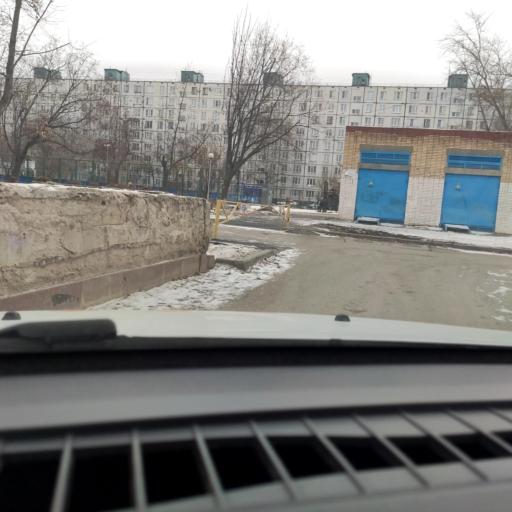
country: RU
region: Samara
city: Tol'yatti
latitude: 53.5335
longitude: 49.2715
